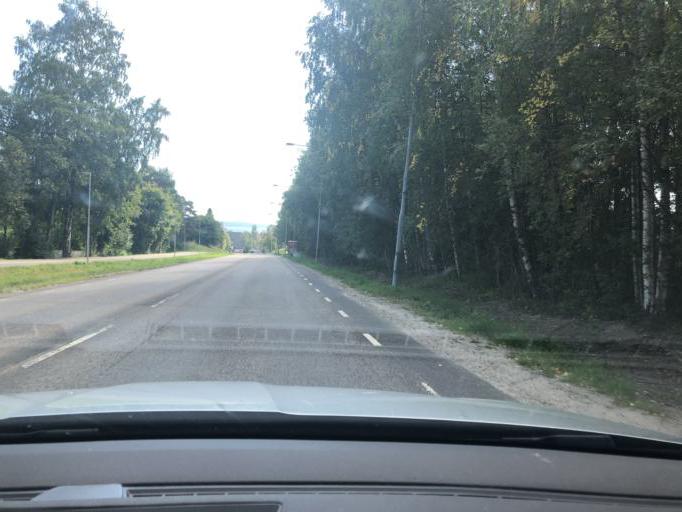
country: SE
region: Vaesternorrland
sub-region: Sundsvalls Kommun
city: Sundsvall
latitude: 62.4027
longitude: 17.3216
